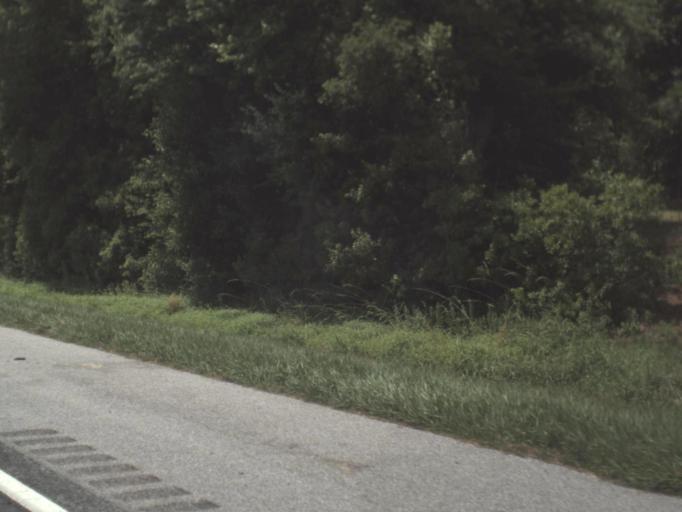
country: US
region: Florida
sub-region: Suwannee County
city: Wellborn
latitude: 30.3191
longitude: -82.8093
